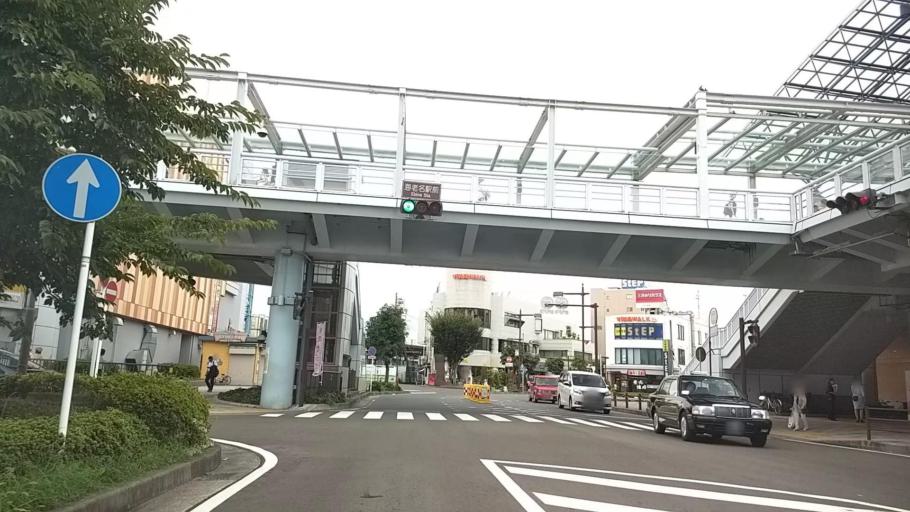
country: JP
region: Kanagawa
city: Atsugi
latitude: 35.4527
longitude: 139.3925
